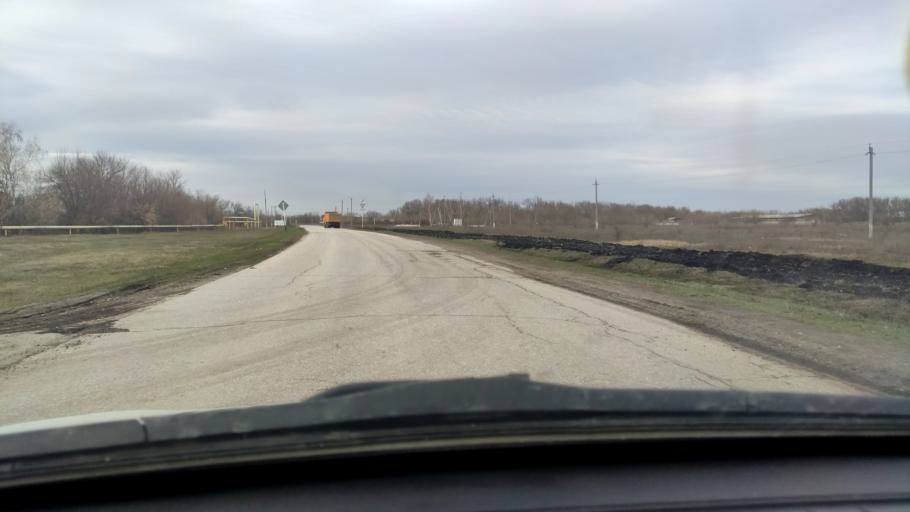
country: RU
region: Samara
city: Mezhdurechensk
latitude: 53.2689
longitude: 49.3008
